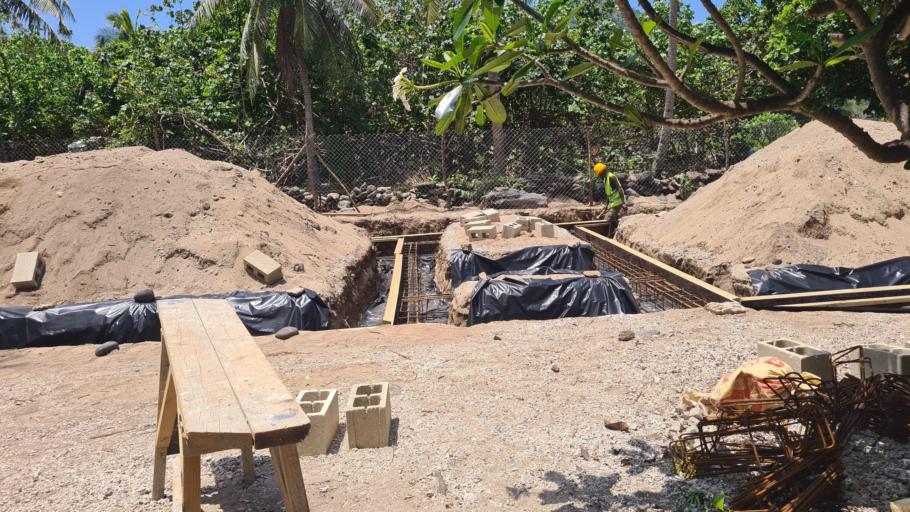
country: VU
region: Shefa
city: Port-Vila
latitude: -17.2568
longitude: 168.4304
